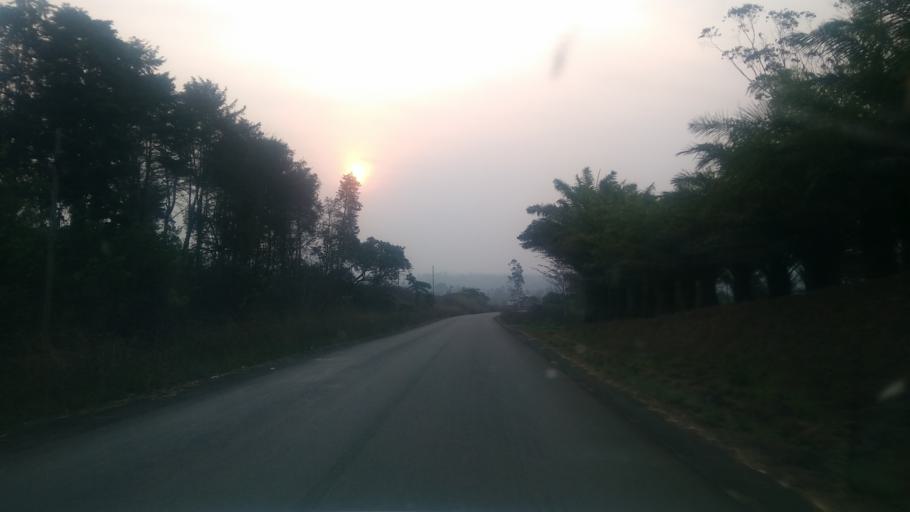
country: CM
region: West
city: Bana
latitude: 5.1621
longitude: 10.2430
